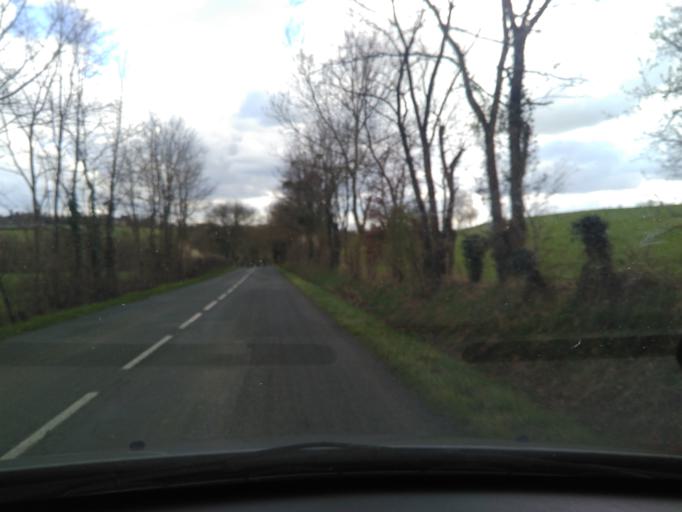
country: FR
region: Pays de la Loire
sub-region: Departement de la Vendee
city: Sainte-Cecile
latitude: 46.6883
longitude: -1.1167
